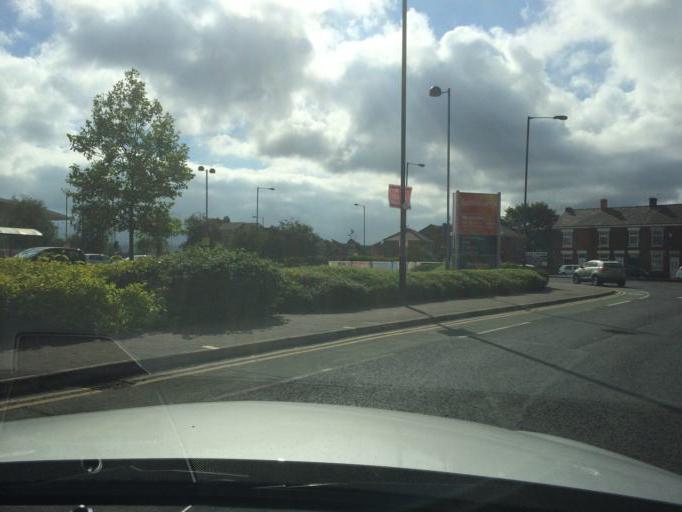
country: GB
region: England
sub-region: Borough of Stockport
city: Hazel Grove
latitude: 53.3844
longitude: -2.1267
